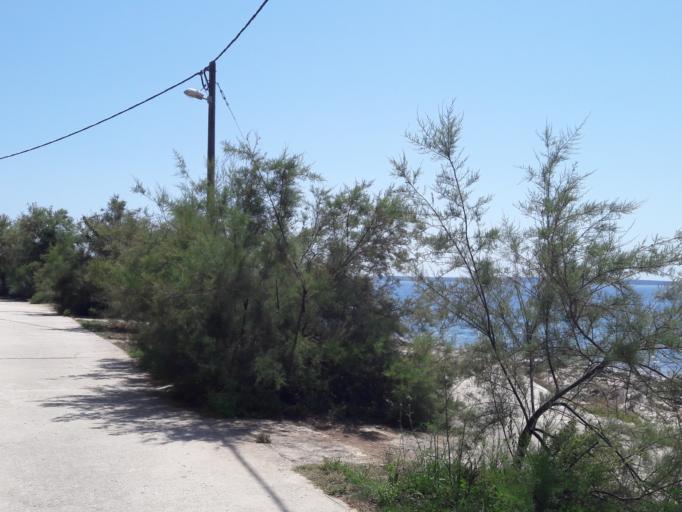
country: HR
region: Licko-Senjska
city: Novalja
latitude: 44.3721
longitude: 14.6920
